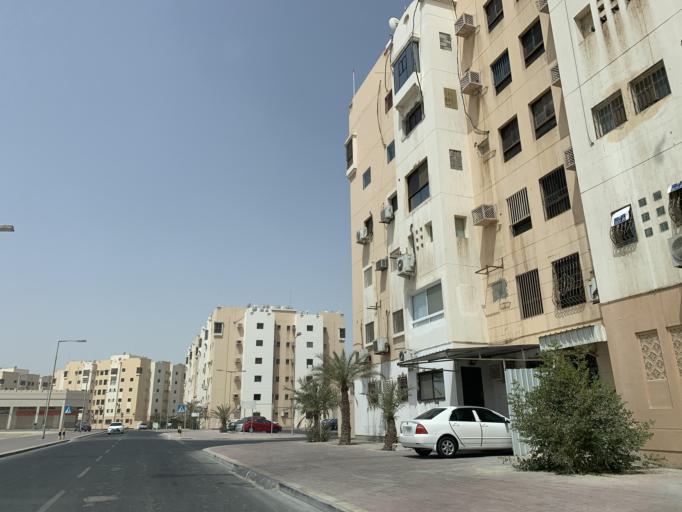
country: BH
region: Northern
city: Madinat `Isa
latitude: 26.1711
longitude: 50.5219
